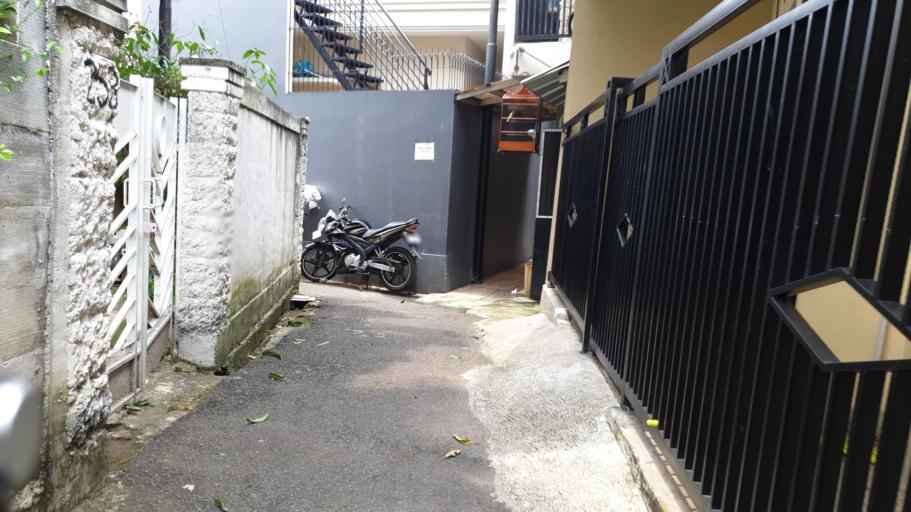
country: ID
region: West Java
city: Pamulang
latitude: -6.3037
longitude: 106.7808
